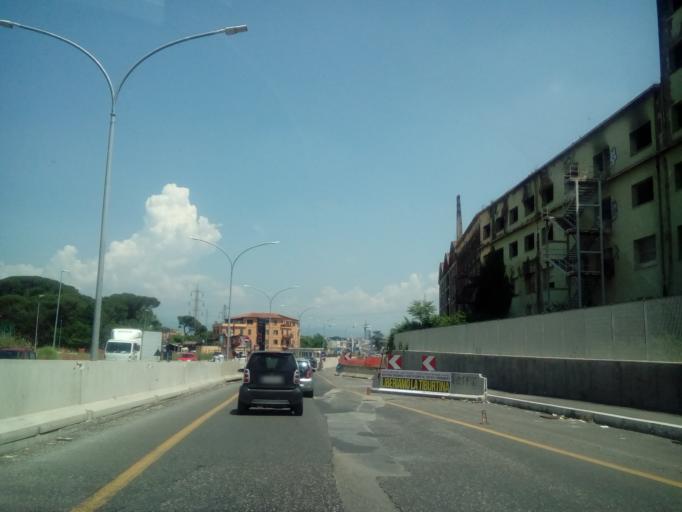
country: IT
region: Latium
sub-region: Citta metropolitana di Roma Capitale
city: Colle Verde
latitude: 41.9322
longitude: 12.5821
